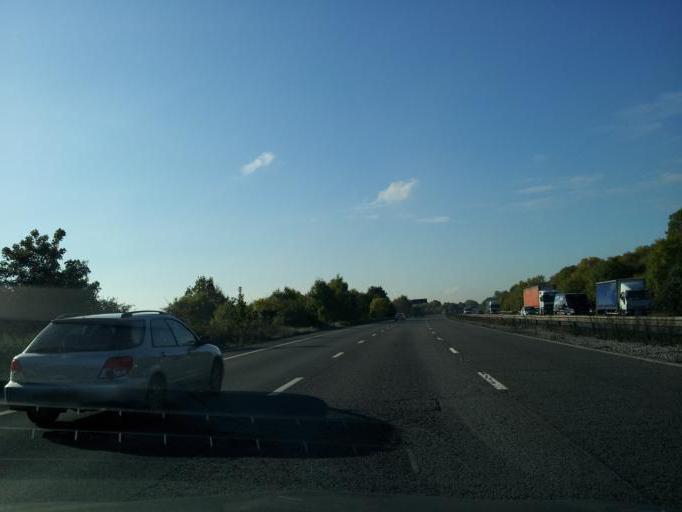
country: GB
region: England
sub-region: Leicestershire
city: Cosby
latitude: 52.5194
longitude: -1.1767
